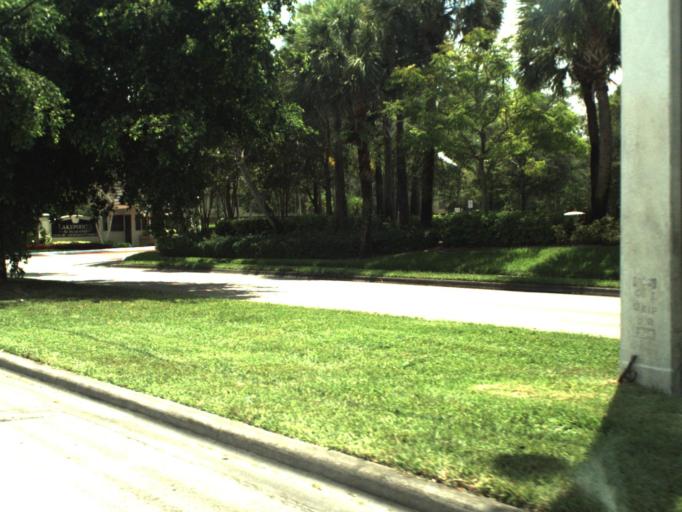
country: US
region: Florida
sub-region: Broward County
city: Plantation
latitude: 26.1405
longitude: -80.2570
